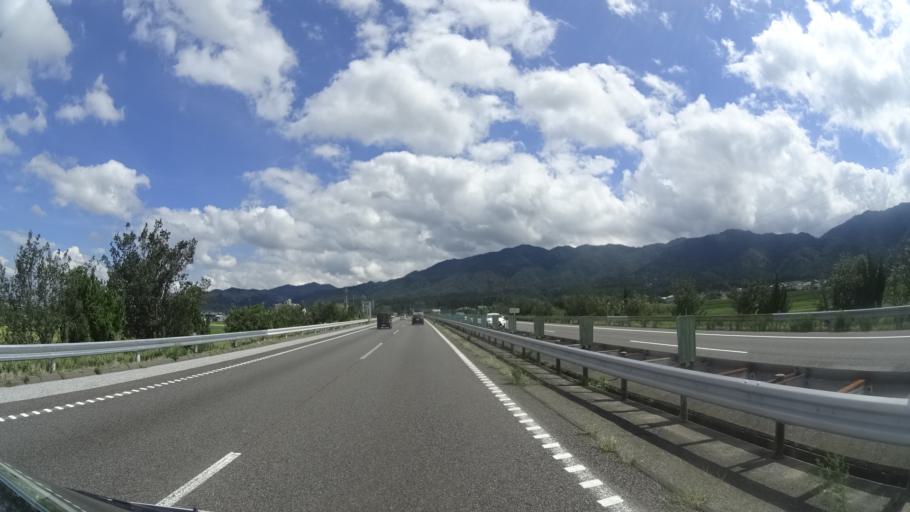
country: JP
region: Shiga Prefecture
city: Youkaichi
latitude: 35.1235
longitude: 136.2691
